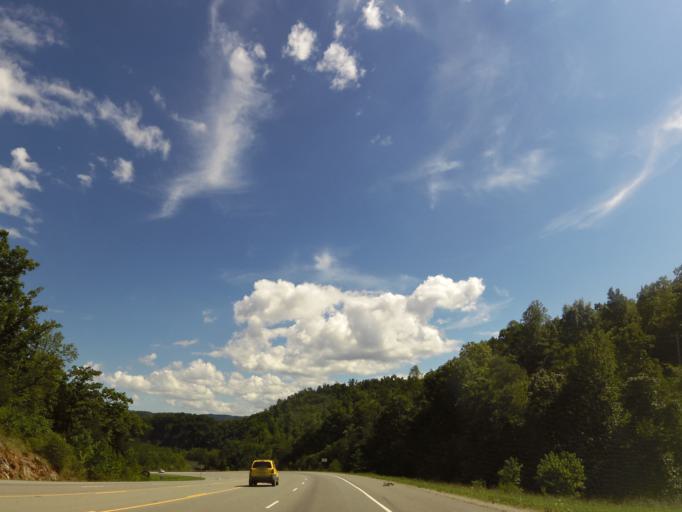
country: US
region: Tennessee
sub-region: Claiborne County
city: Tazewell
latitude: 36.4052
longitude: -83.4625
